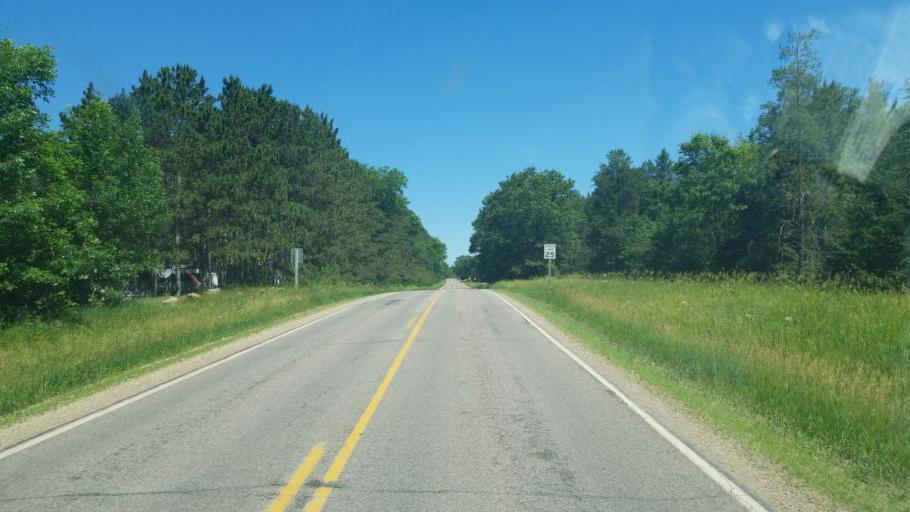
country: US
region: Wisconsin
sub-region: Adams County
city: Adams
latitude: 43.9051
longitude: -89.9377
